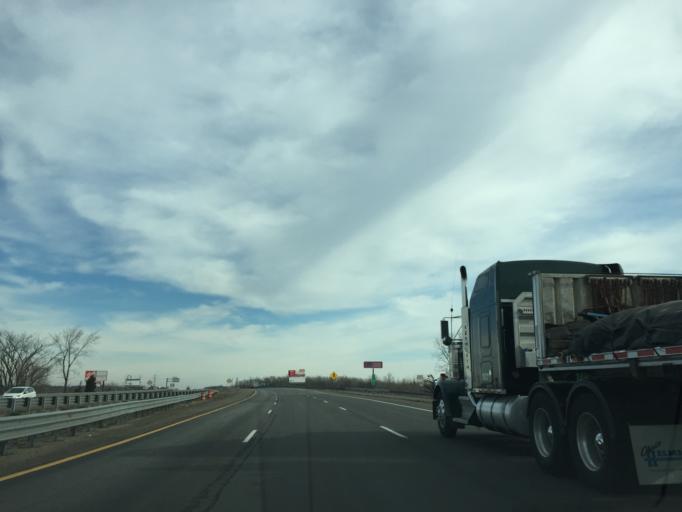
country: US
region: Michigan
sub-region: Berrien County
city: Fair Plain
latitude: 42.0793
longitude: -86.4167
